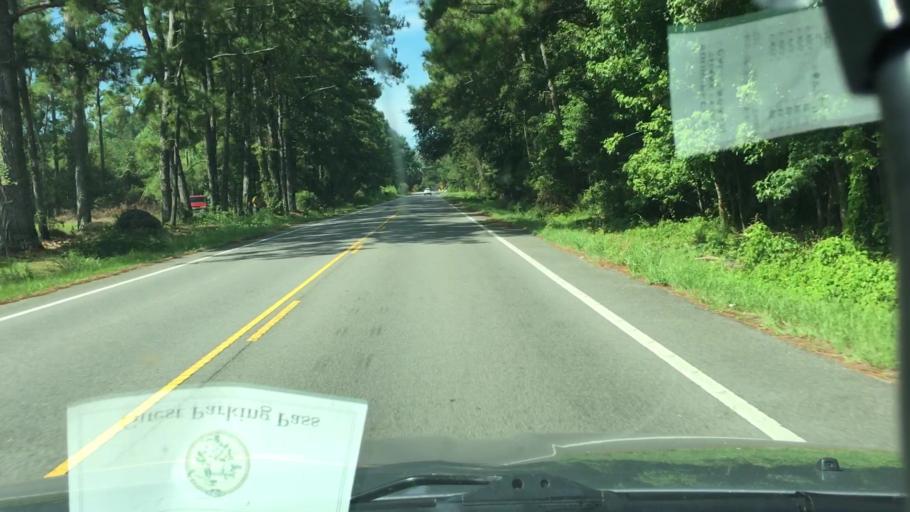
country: US
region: South Carolina
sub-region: Beaufort County
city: Beaufort
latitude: 32.4035
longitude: -80.5350
